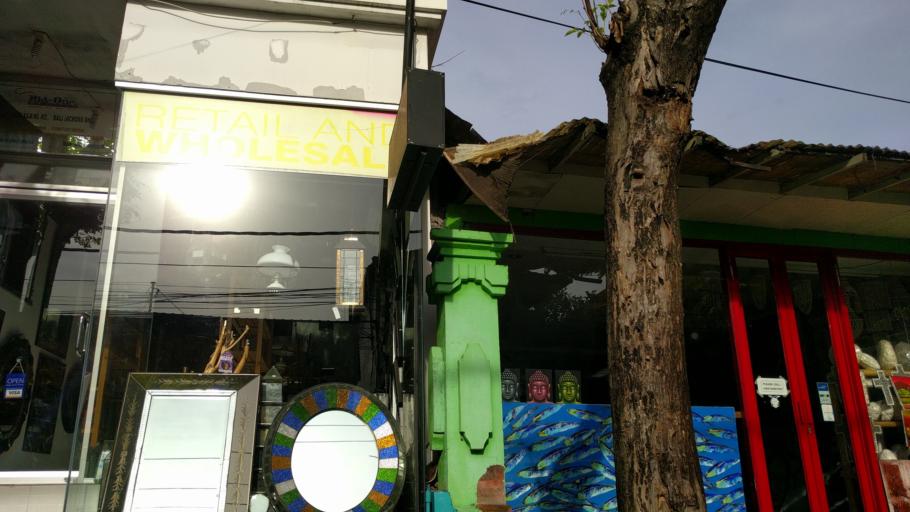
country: ID
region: Bali
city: Kuta
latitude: -8.7018
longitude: 115.1700
